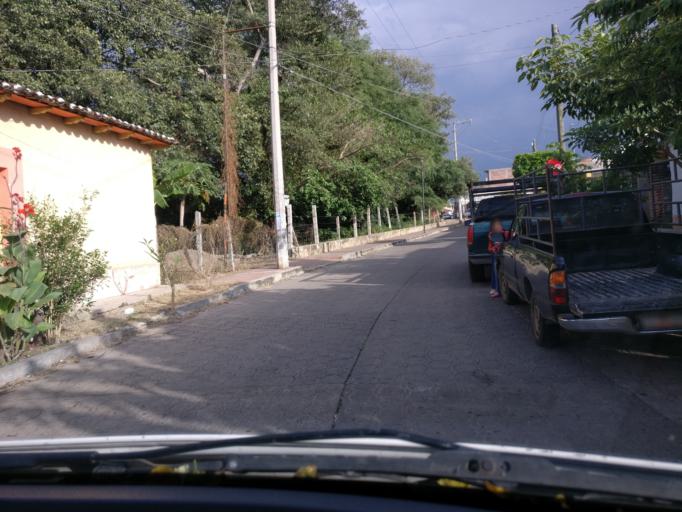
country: MX
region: Chiapas
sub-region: Chiapa de Corzo
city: Las Flechas
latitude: 16.7100
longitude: -93.0226
